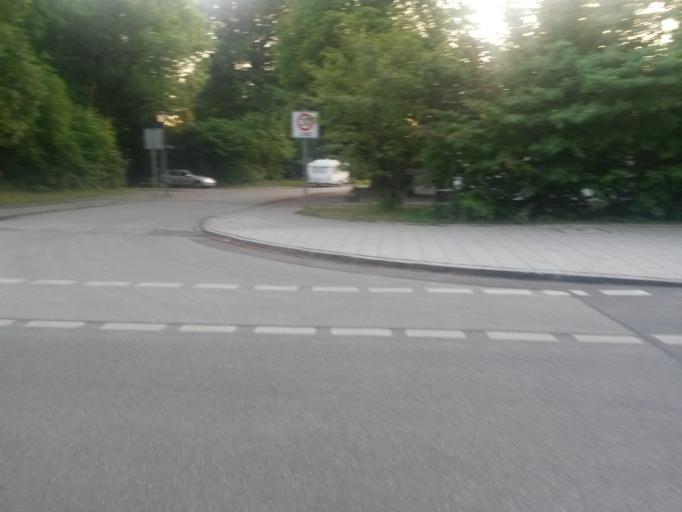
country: DE
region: Bavaria
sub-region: Upper Bavaria
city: Bogenhausen
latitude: 48.1139
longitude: 11.6134
